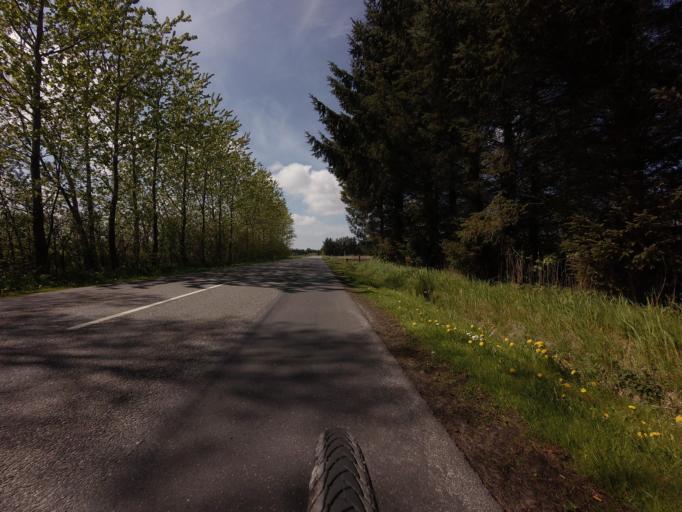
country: DK
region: North Denmark
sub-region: Jammerbugt Kommune
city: Brovst
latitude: 57.1428
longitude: 9.5239
